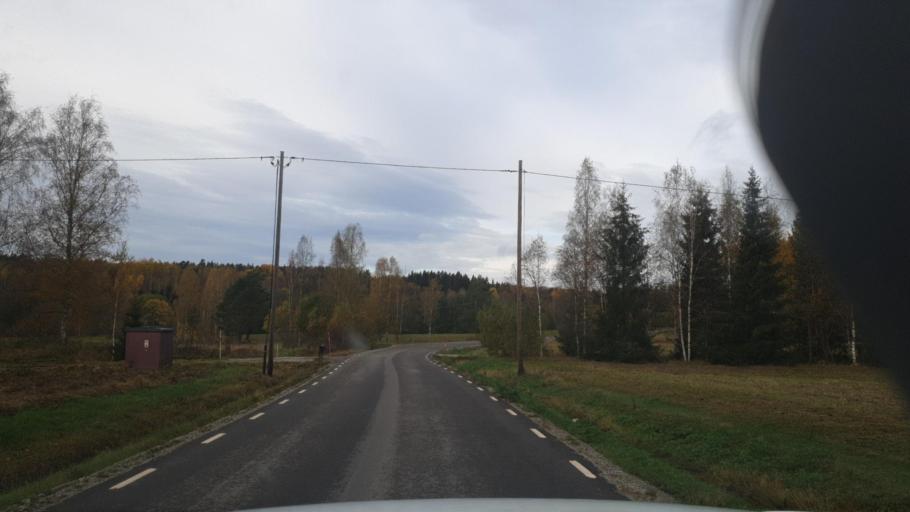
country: SE
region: Vaermland
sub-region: Sunne Kommun
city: Sunne
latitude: 59.6685
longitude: 12.9085
